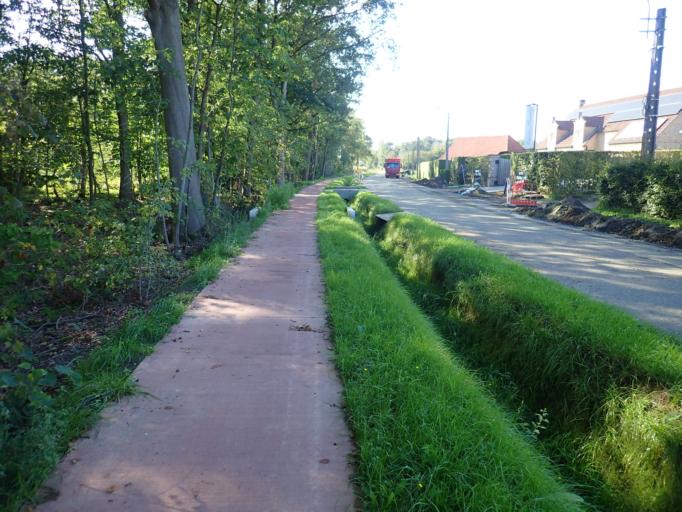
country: BE
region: Flanders
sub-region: Provincie Antwerpen
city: Nijlen
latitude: 51.1486
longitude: 4.7104
